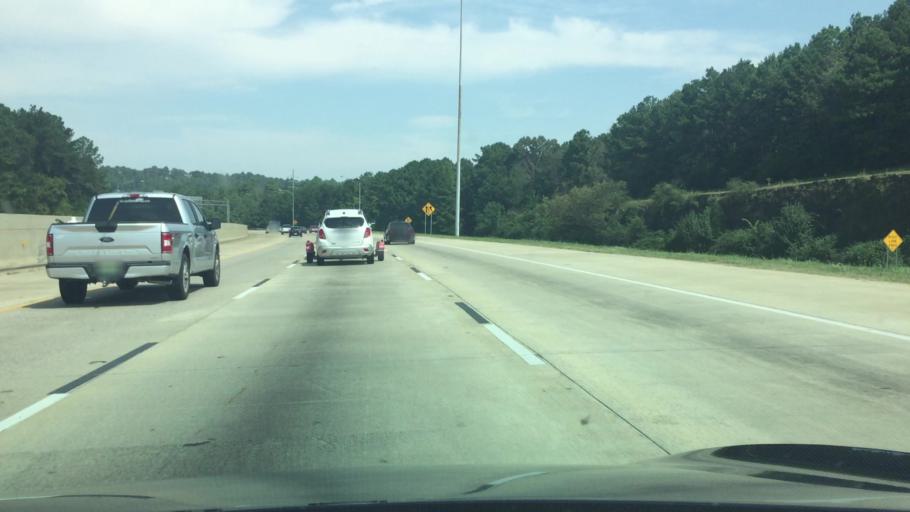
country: US
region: Alabama
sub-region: Jefferson County
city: Hoover
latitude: 33.3981
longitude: -86.7859
